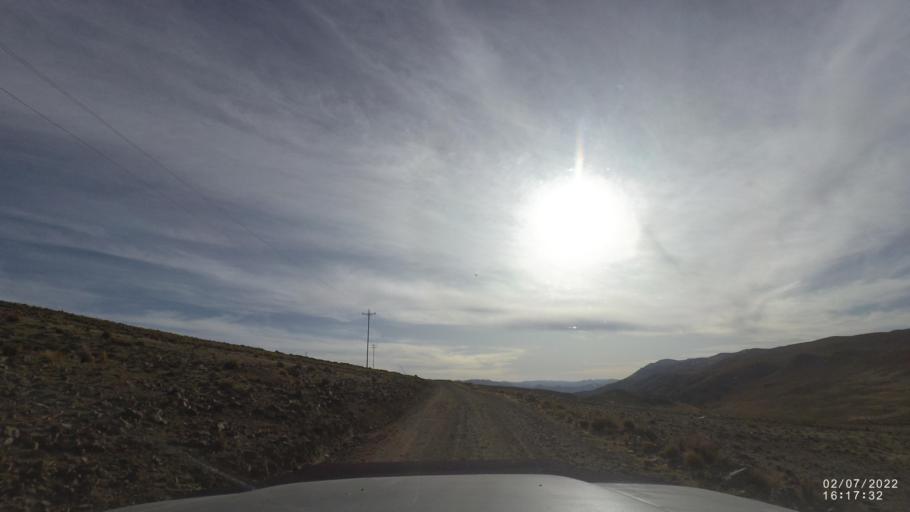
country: BO
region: Cochabamba
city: Irpa Irpa
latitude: -17.9251
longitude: -66.4378
